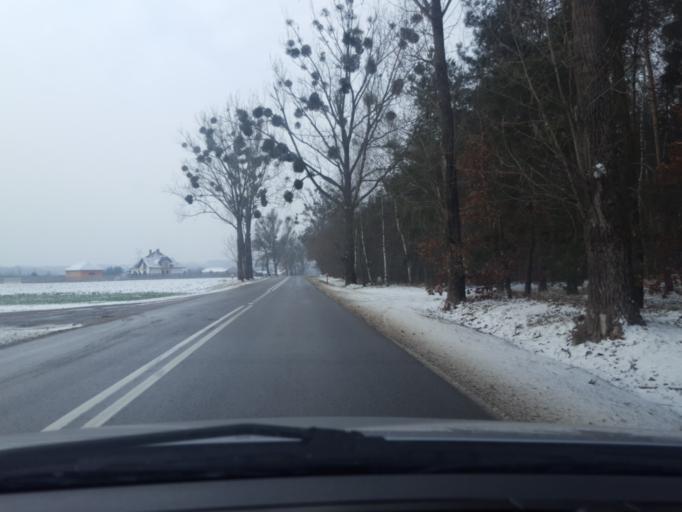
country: PL
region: Lodz Voivodeship
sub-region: Powiat brzezinski
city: Brzeziny
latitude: 51.8329
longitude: 19.7996
